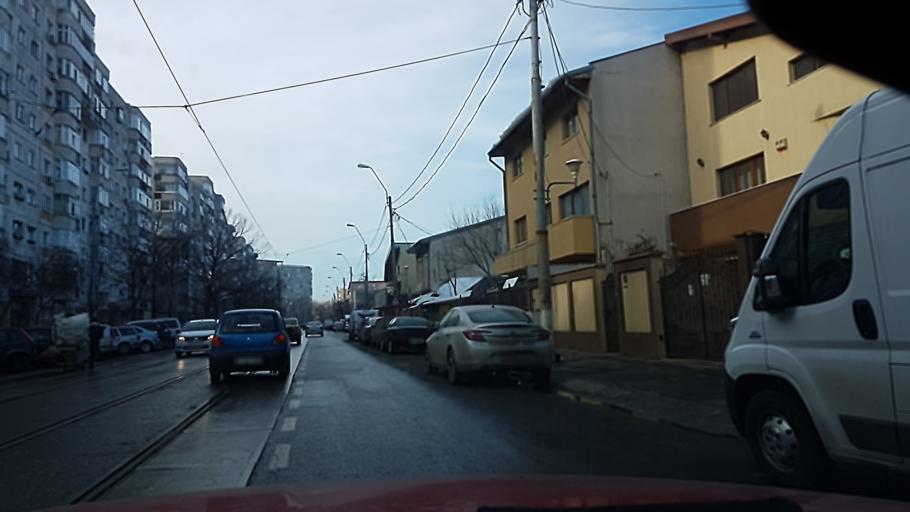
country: RO
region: Ilfov
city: Dobroesti
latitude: 44.4280
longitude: 26.1771
